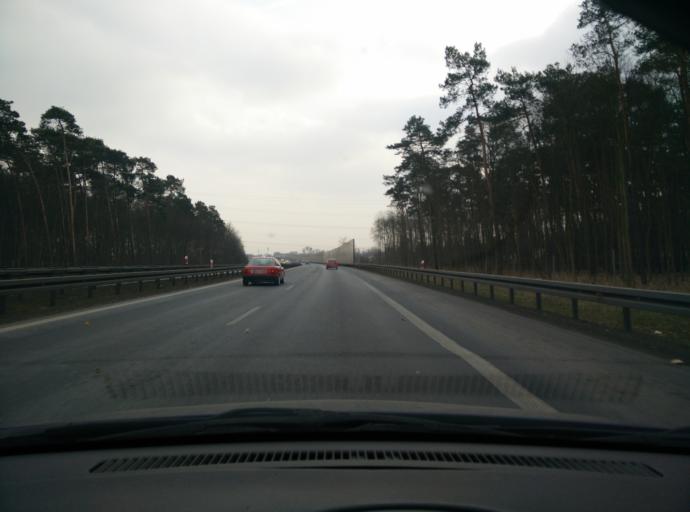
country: PL
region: Greater Poland Voivodeship
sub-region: Powiat poznanski
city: Kornik
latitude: 52.2742
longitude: 17.0646
